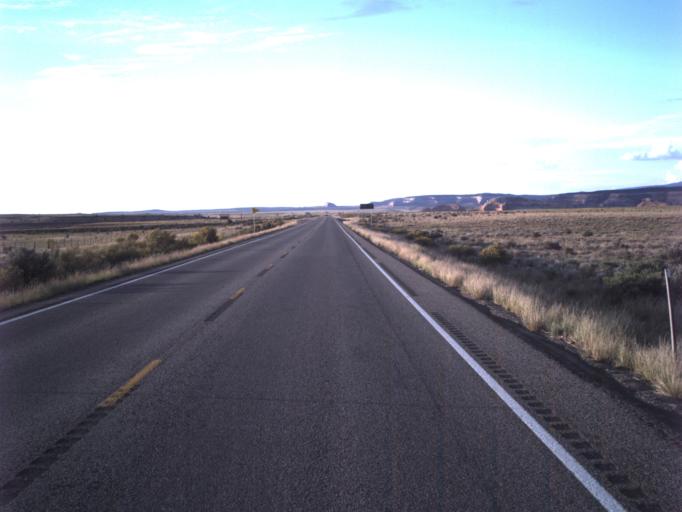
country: US
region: Utah
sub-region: San Juan County
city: Monticello
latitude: 38.1681
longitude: -109.3783
